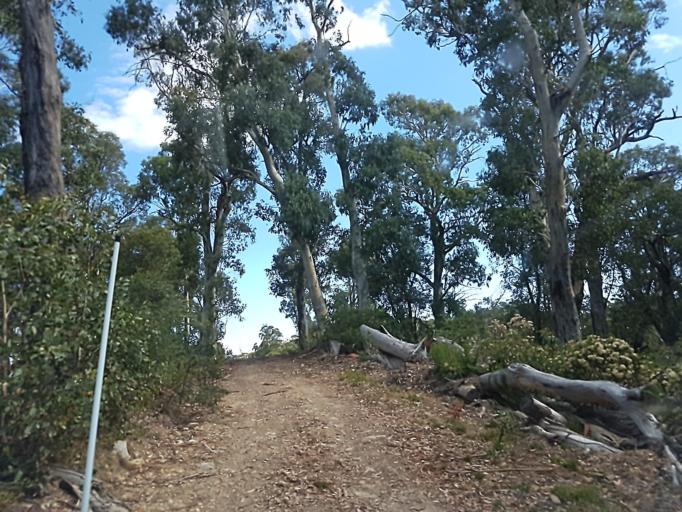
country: AU
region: Victoria
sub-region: Alpine
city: Mount Beauty
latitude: -36.9170
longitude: 146.9989
